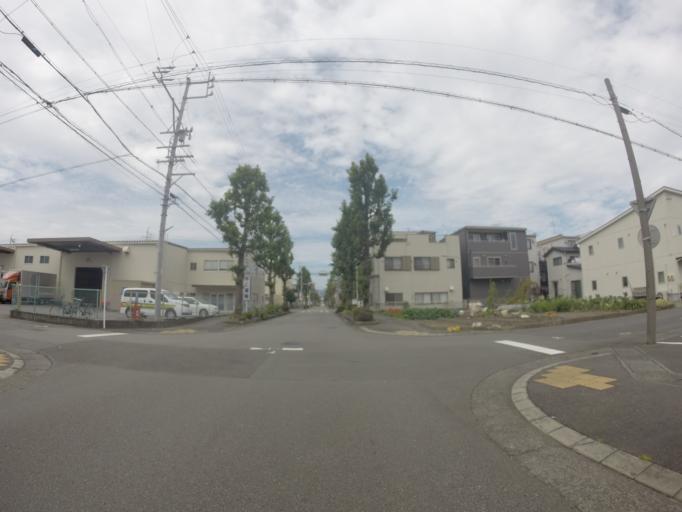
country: JP
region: Shizuoka
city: Shizuoka-shi
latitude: 34.9485
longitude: 138.4142
